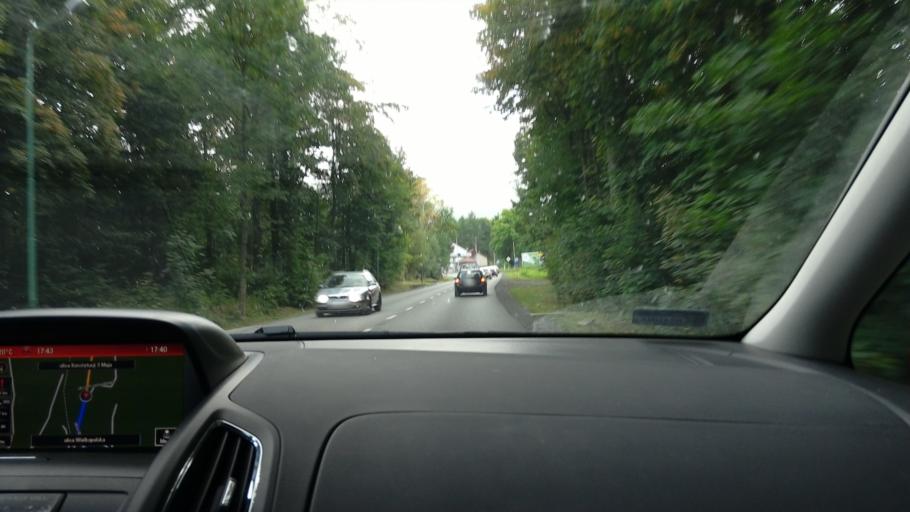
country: PL
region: Lower Silesian Voivodeship
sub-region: Powiat jeleniogorski
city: Karpacz
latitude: 50.7887
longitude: 15.7600
